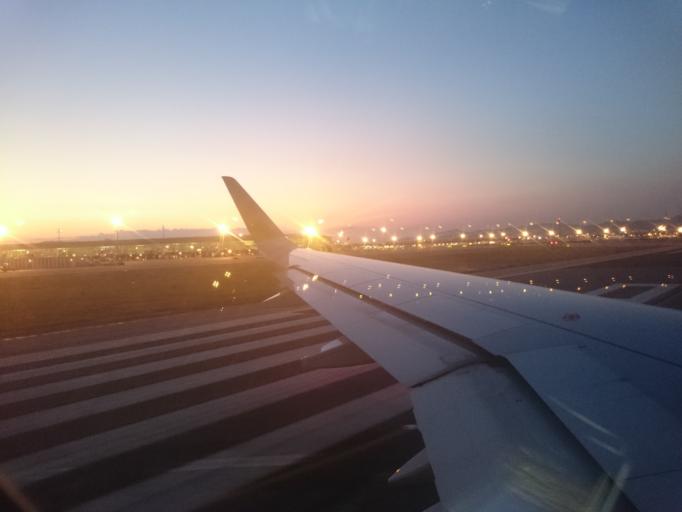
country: ES
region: Catalonia
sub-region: Provincia de Barcelona
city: El Prat de Llobregat
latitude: 41.2878
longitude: 2.0850
